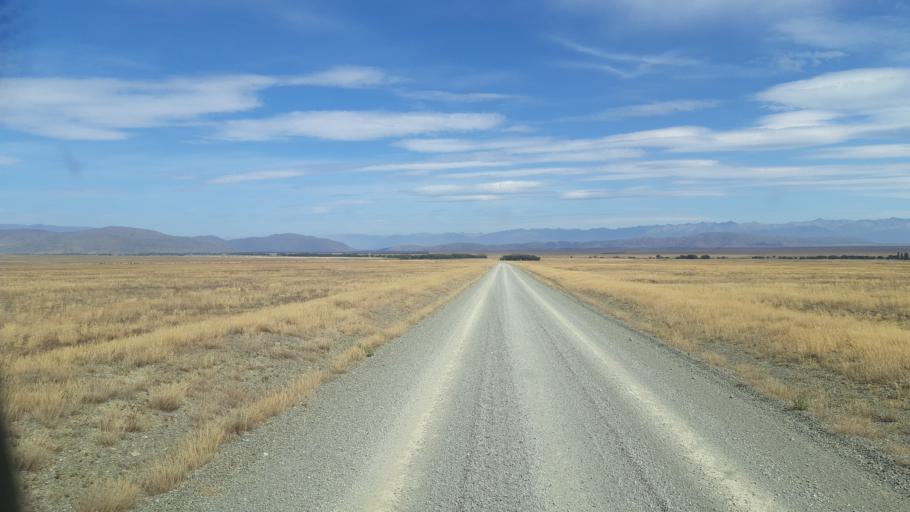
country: NZ
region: Canterbury
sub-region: Timaru District
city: Pleasant Point
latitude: -44.1949
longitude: 170.5380
